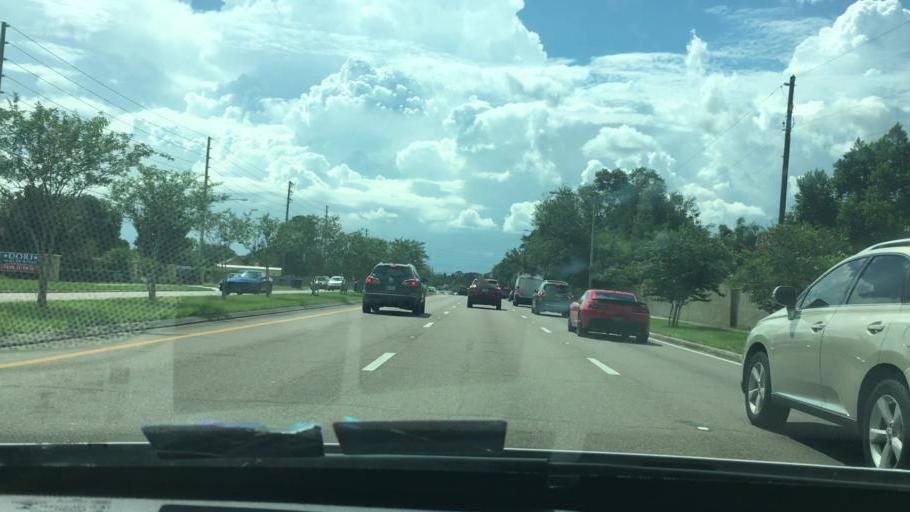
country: US
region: Florida
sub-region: Seminole County
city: Goldenrod
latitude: 28.5983
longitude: -81.2653
